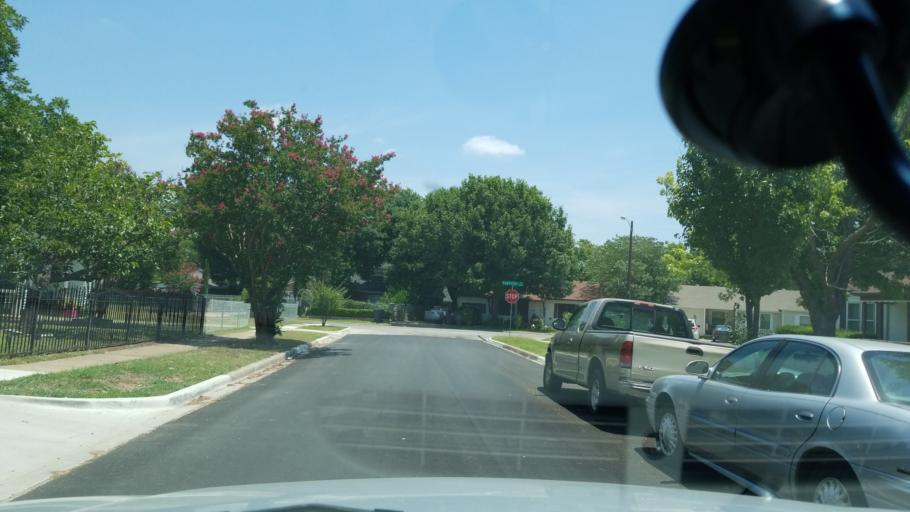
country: US
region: Texas
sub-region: Dallas County
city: Cockrell Hill
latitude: 32.7257
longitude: -96.8644
